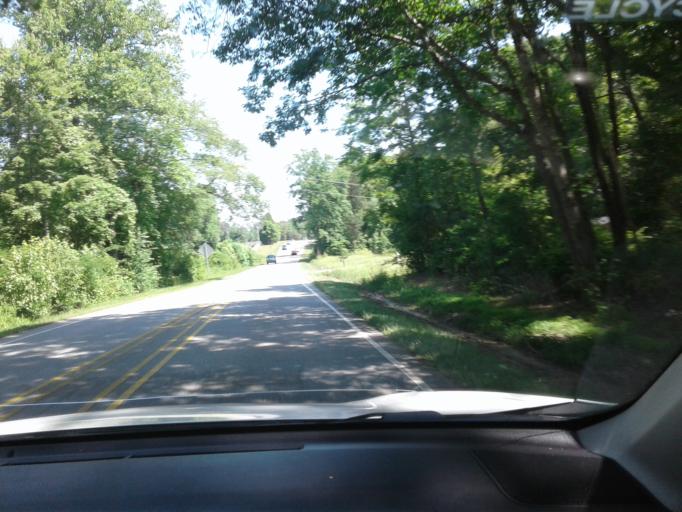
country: US
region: North Carolina
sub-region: Wake County
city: Holly Springs
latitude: 35.6264
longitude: -78.8405
